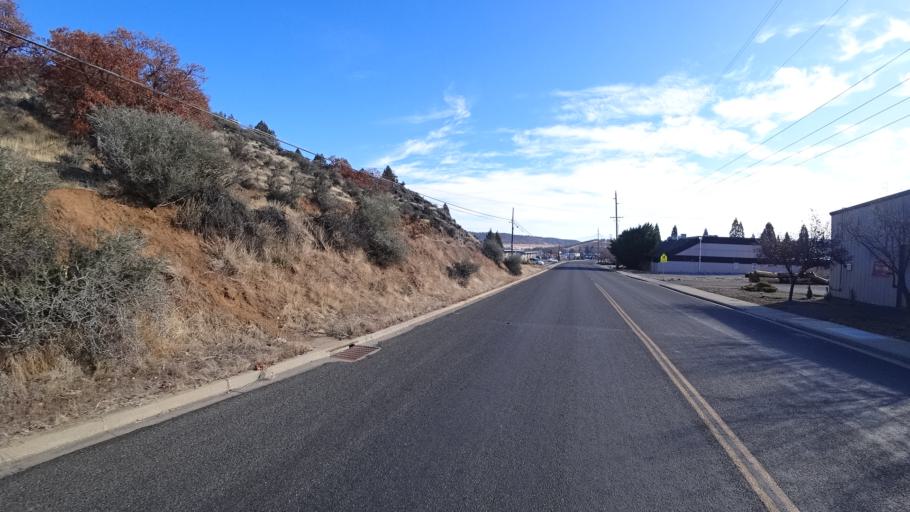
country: US
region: California
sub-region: Siskiyou County
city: Yreka
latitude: 41.7118
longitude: -122.6465
